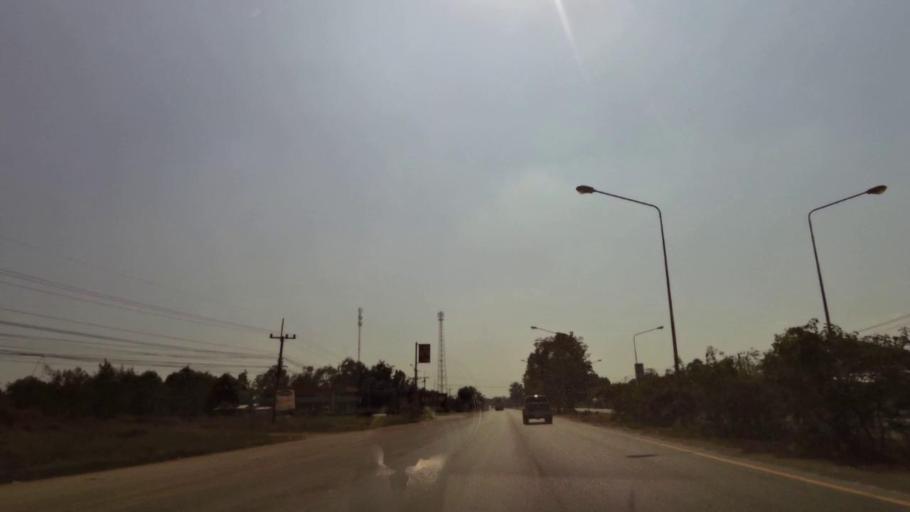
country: TH
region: Phichit
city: Wachira Barami
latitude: 16.3480
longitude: 100.1284
